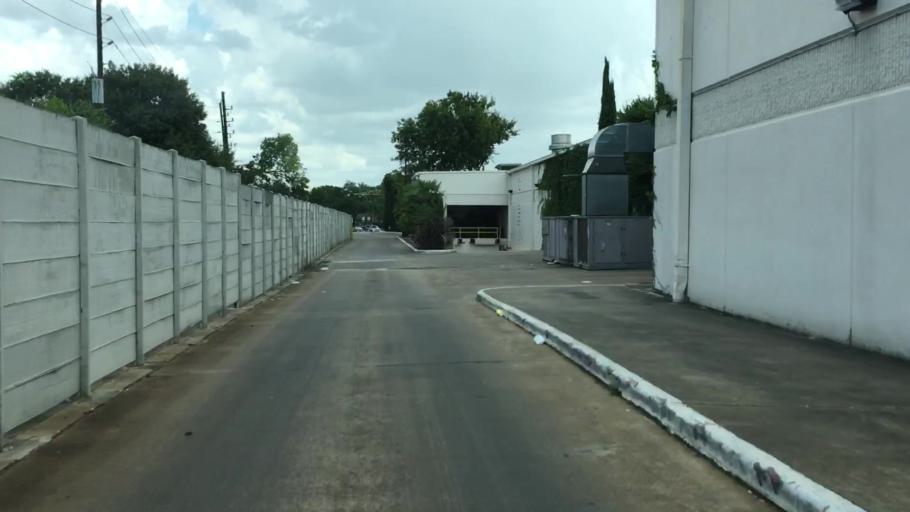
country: US
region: Texas
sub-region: Fort Bend County
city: Meadows Place
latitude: 29.6487
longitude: -95.5771
